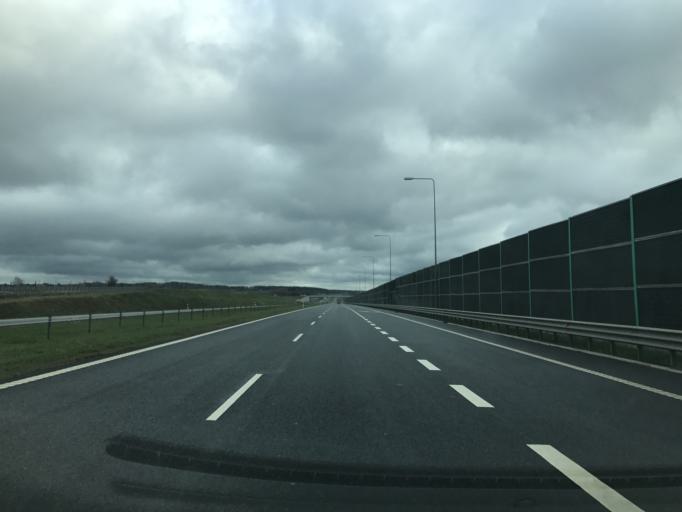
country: PL
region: Warmian-Masurian Voivodeship
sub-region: Powiat olsztynski
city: Olsztynek
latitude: 53.5729
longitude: 20.2599
